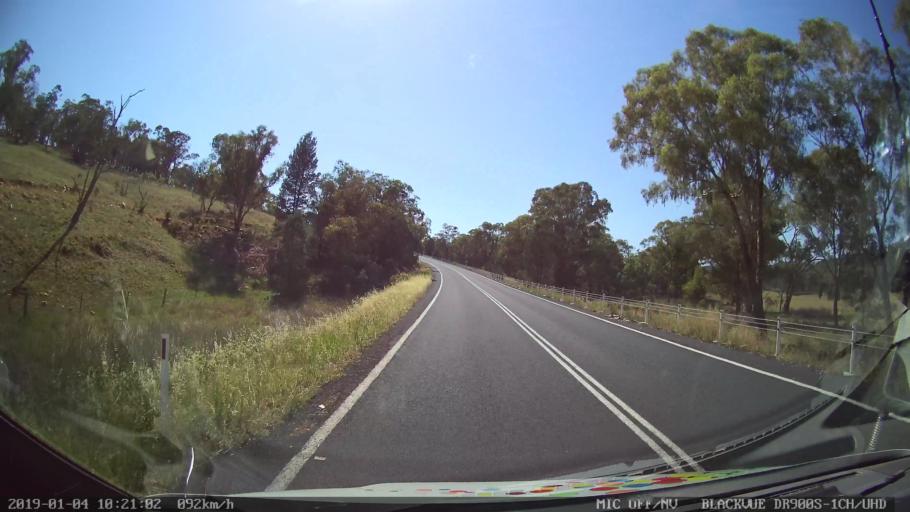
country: AU
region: New South Wales
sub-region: Cabonne
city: Canowindra
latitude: -33.3730
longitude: 148.5045
